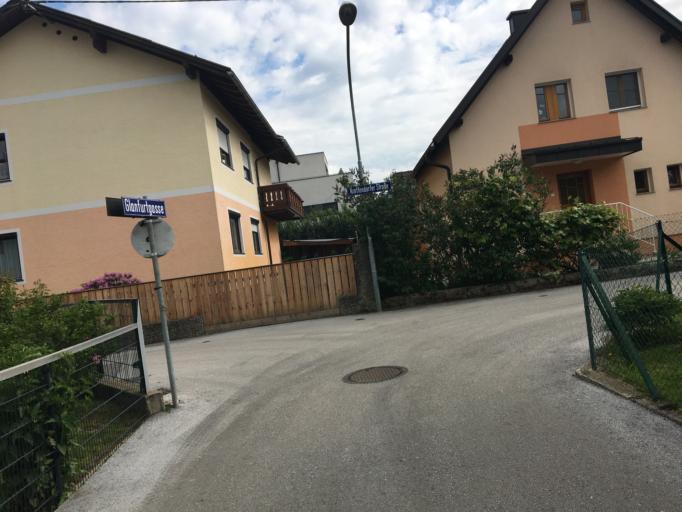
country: AT
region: Carinthia
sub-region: Klagenfurt am Woerthersee
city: Klagenfurt am Woerthersee
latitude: 46.5970
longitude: 14.2728
